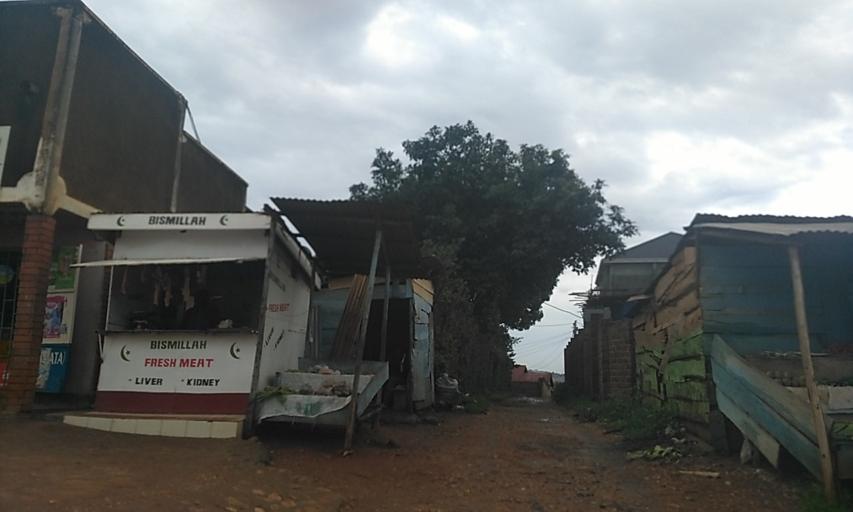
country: UG
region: Central Region
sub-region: Wakiso District
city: Bweyogerere
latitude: 0.3574
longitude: 32.6655
